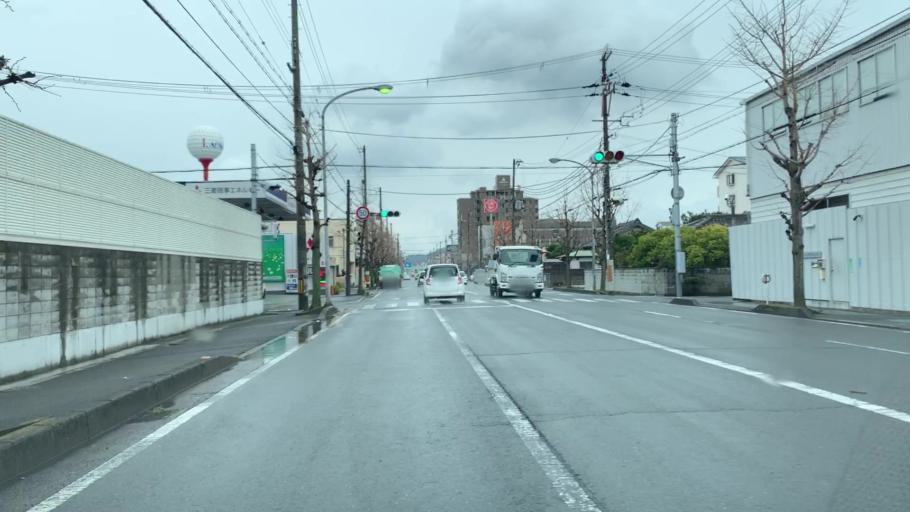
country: JP
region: Wakayama
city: Wakayama-shi
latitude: 34.2234
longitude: 135.1596
